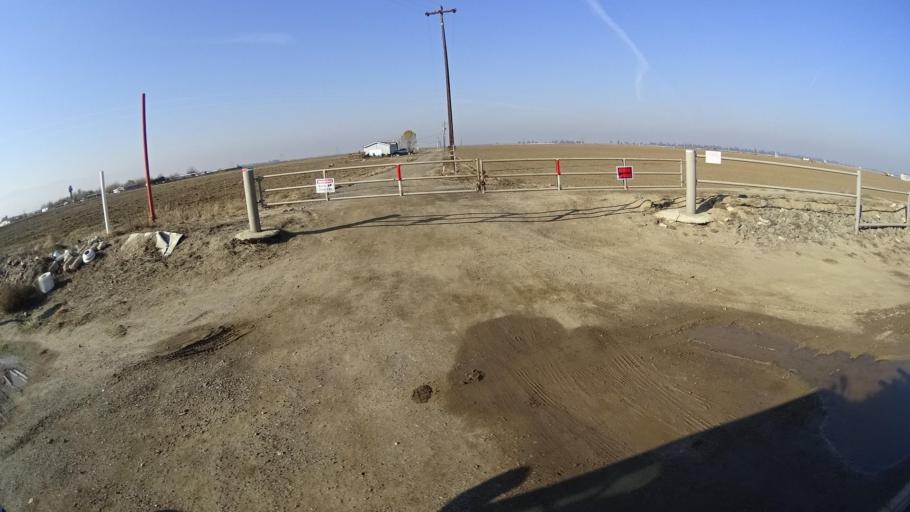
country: US
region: California
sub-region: Kern County
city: Weedpatch
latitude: 35.1654
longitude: -118.9679
